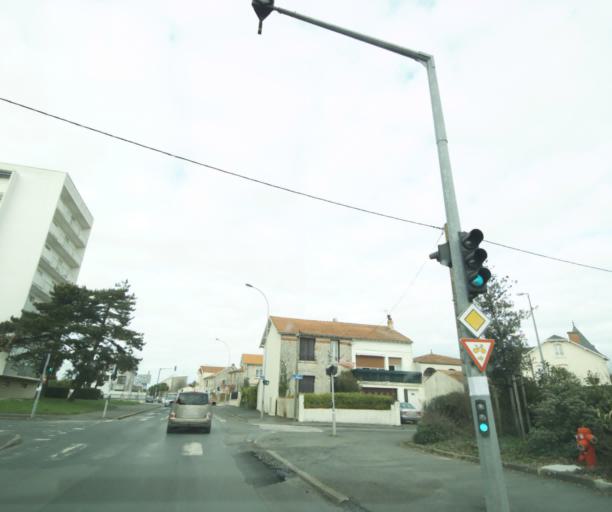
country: FR
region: Poitou-Charentes
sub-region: Departement de la Charente-Maritime
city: La Rochelle
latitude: 46.1666
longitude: -1.1641
